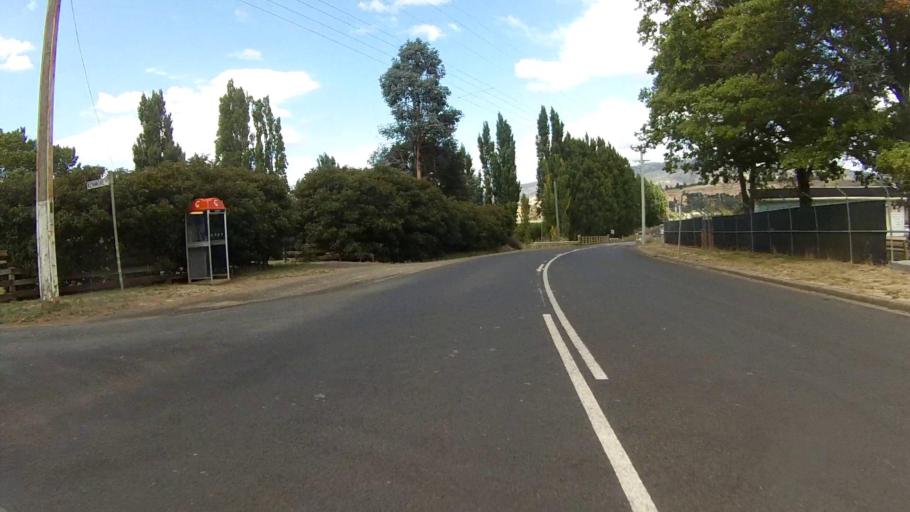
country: AU
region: Tasmania
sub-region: Derwent Valley
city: New Norfolk
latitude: -42.6986
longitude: 146.8907
